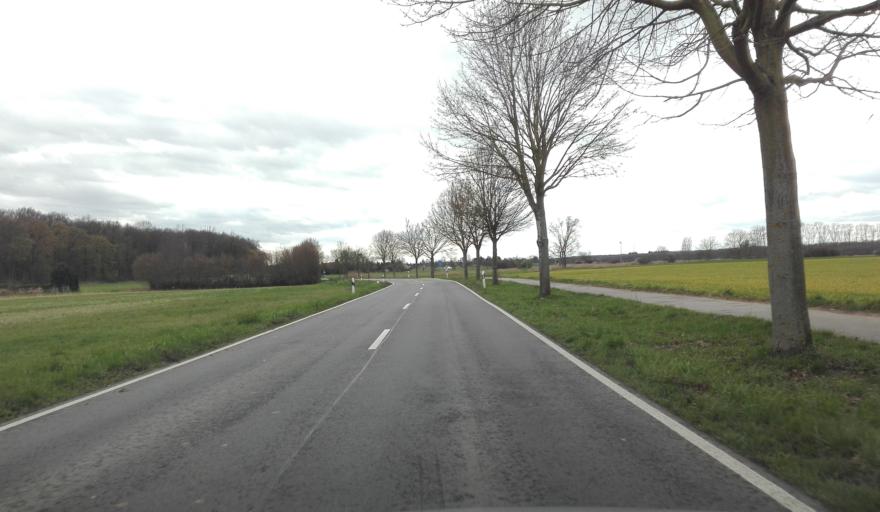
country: DE
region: Hesse
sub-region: Regierungsbezirk Darmstadt
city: Alsbach-Hahnlein
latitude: 49.7161
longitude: 8.5770
